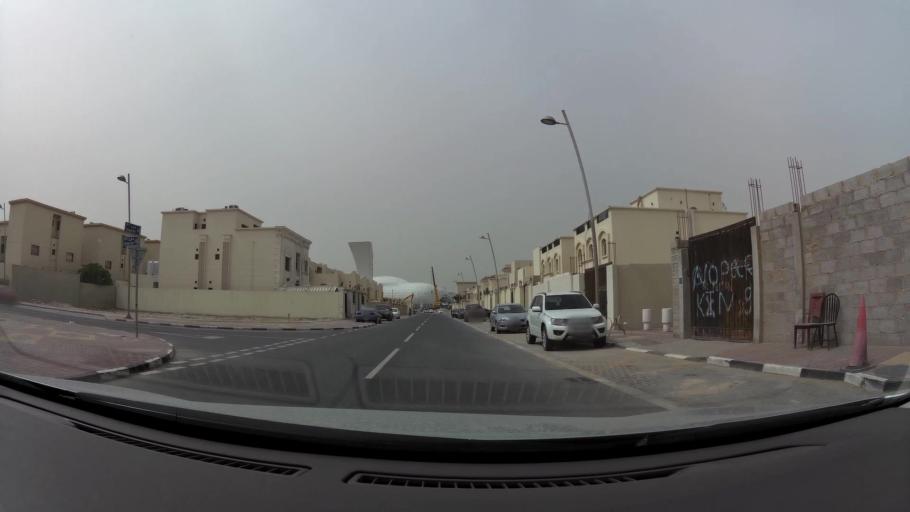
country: QA
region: Baladiyat ad Dawhah
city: Doha
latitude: 25.2351
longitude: 51.5496
